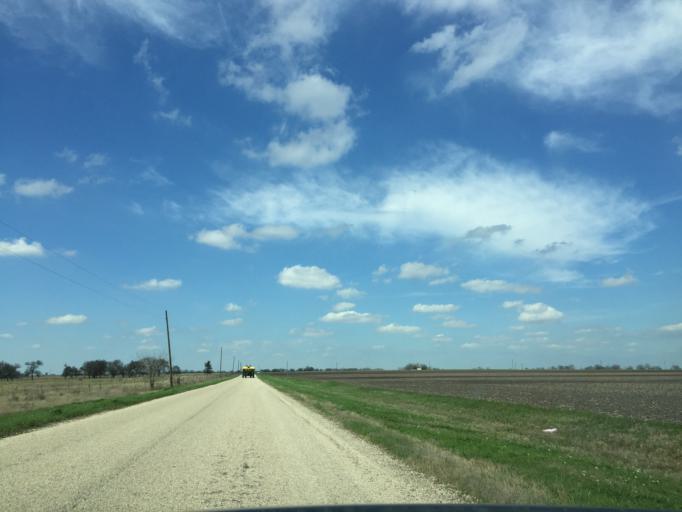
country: US
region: Texas
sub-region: Milam County
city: Thorndale
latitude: 30.5435
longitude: -97.2711
